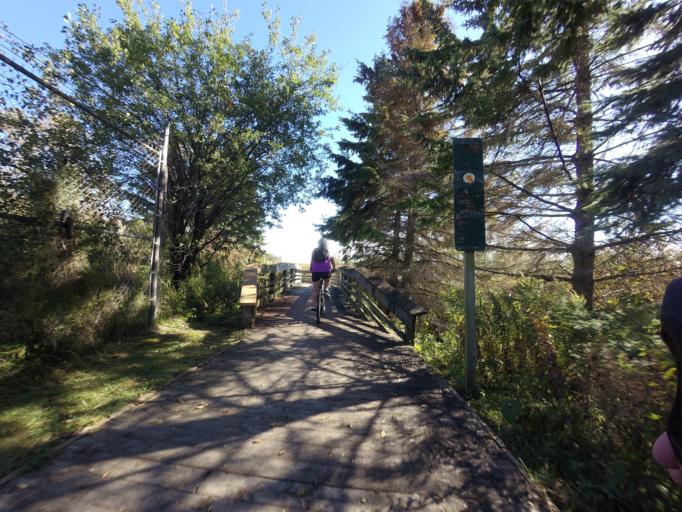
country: CA
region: Ontario
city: Oshawa
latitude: 43.8558
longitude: -78.8874
